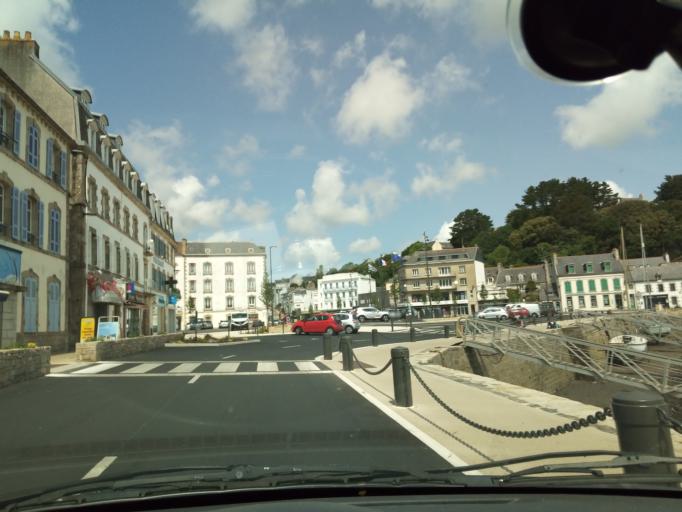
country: FR
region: Brittany
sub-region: Departement du Finistere
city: Audierne
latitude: 48.0224
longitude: -4.5387
